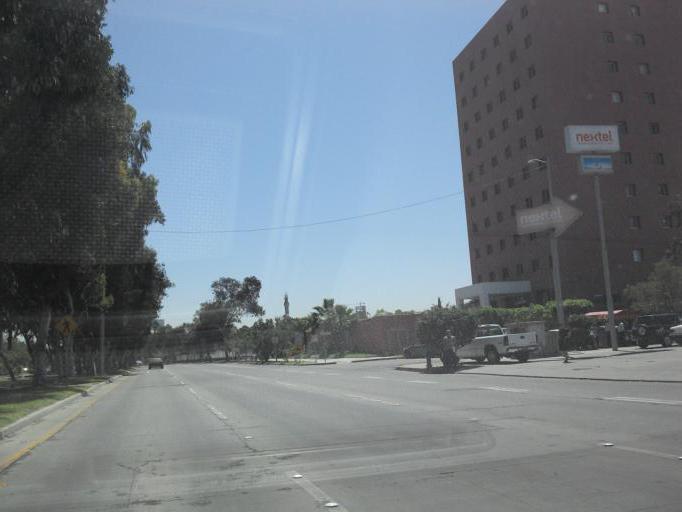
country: MX
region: Baja California
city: Tijuana
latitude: 32.5192
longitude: -117.0082
